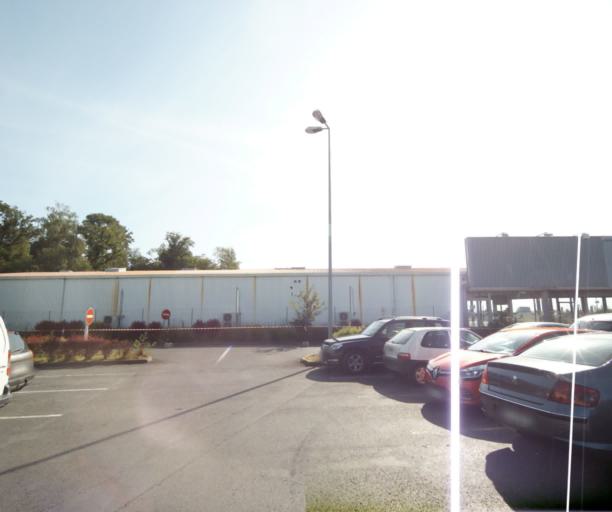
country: FR
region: Champagne-Ardenne
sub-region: Departement des Ardennes
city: La Francheville
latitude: 49.7409
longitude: 4.7025
